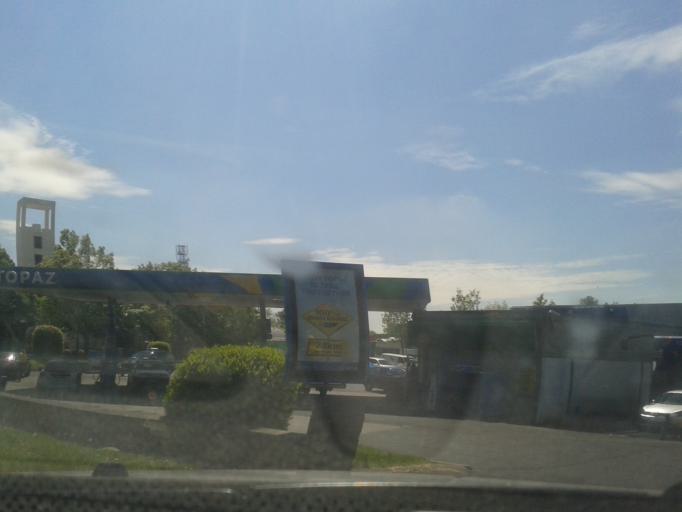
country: IE
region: Leinster
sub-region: Fingal County
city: Blanchardstown
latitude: 53.3855
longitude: -6.3961
